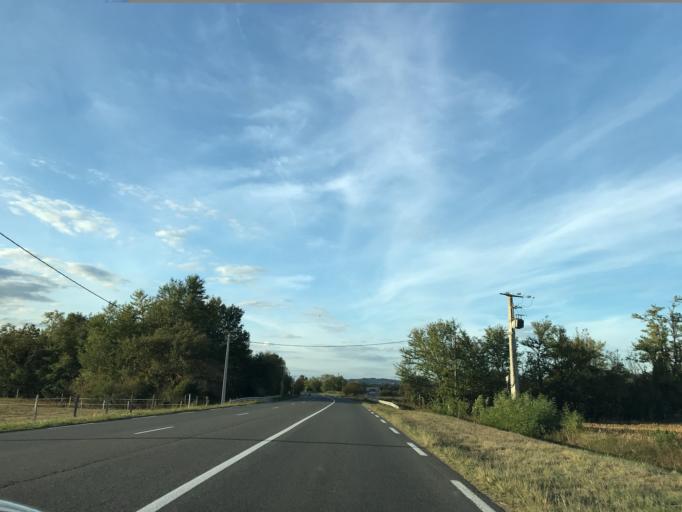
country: FR
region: Auvergne
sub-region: Departement de l'Allier
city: Saint-Yorre
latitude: 46.0378
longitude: 3.4751
